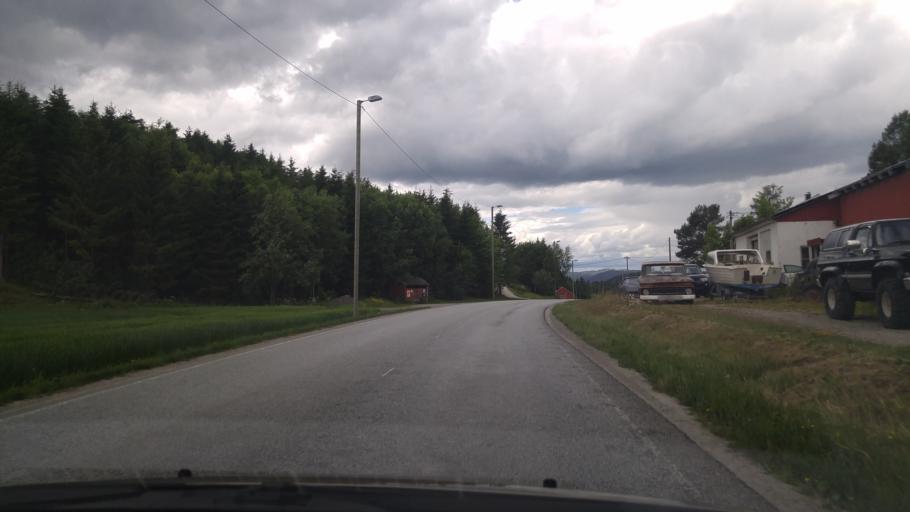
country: NO
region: Nord-Trondelag
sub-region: Steinkjer
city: Steinkjer
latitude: 64.0965
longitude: 11.4507
